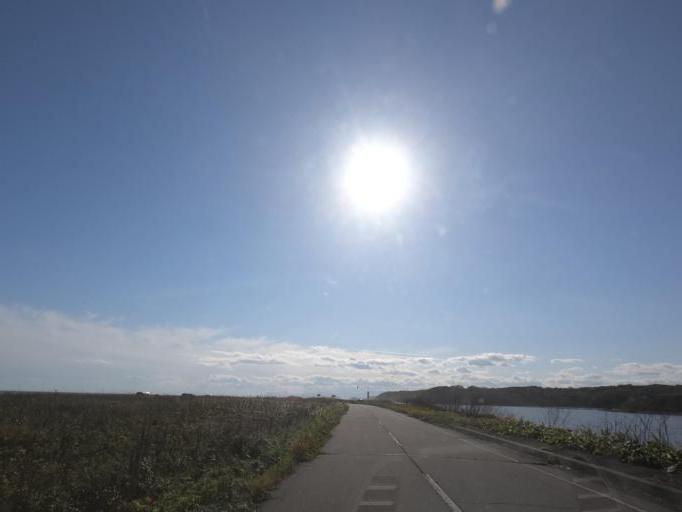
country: JP
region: Hokkaido
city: Obihiro
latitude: 42.5817
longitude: 143.5310
